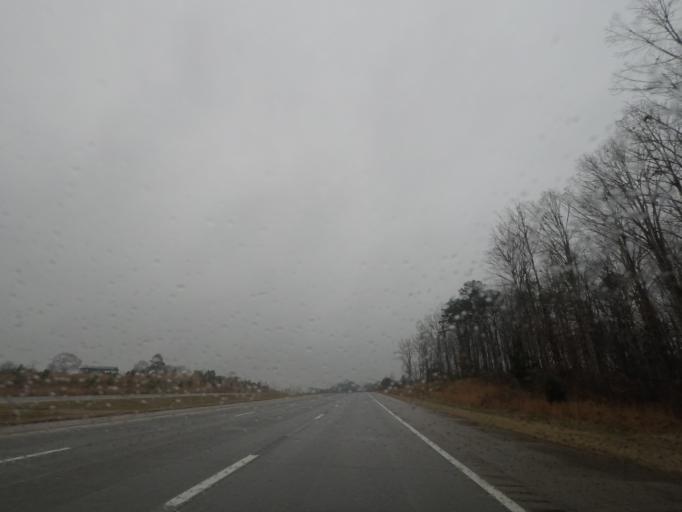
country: US
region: North Carolina
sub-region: Wake County
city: Green Level
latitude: 35.7618
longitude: -78.8901
